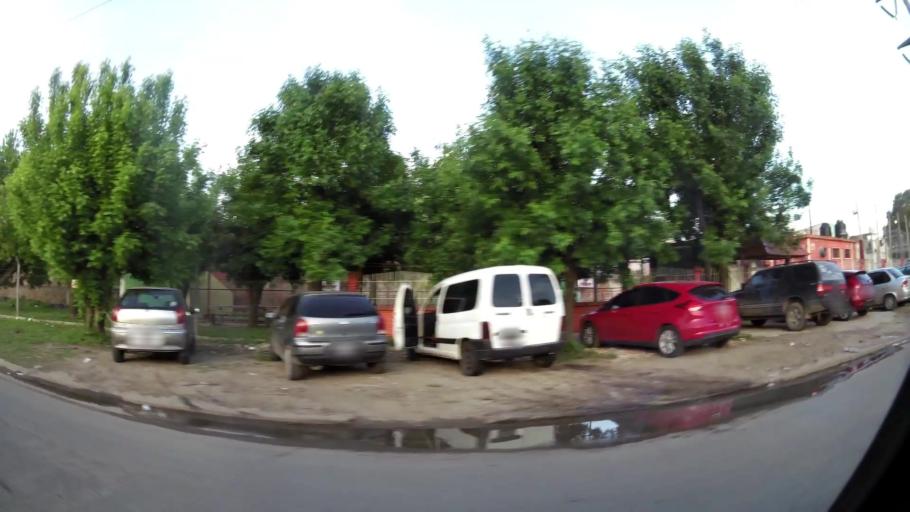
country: AR
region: Buenos Aires
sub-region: Partido de Almirante Brown
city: Adrogue
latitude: -34.7802
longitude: -58.3190
